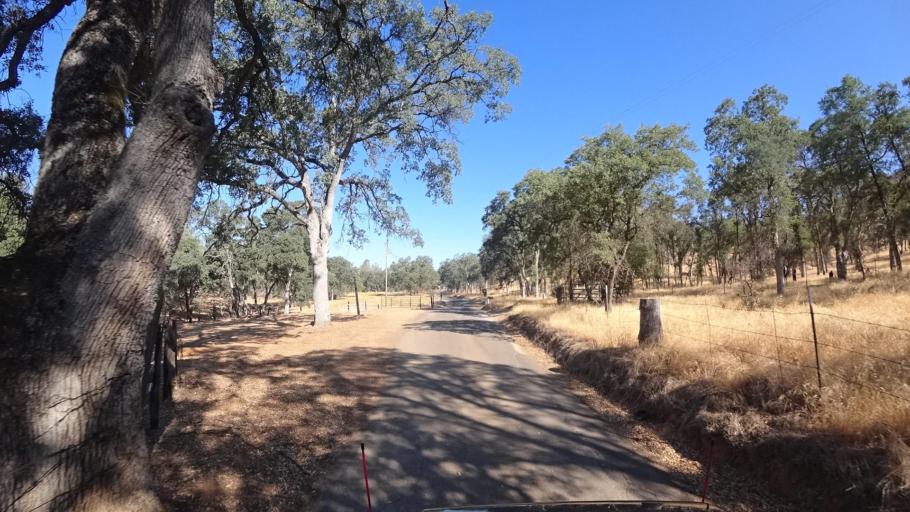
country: US
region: California
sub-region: Mariposa County
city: Mariposa
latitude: 37.6031
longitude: -120.1986
